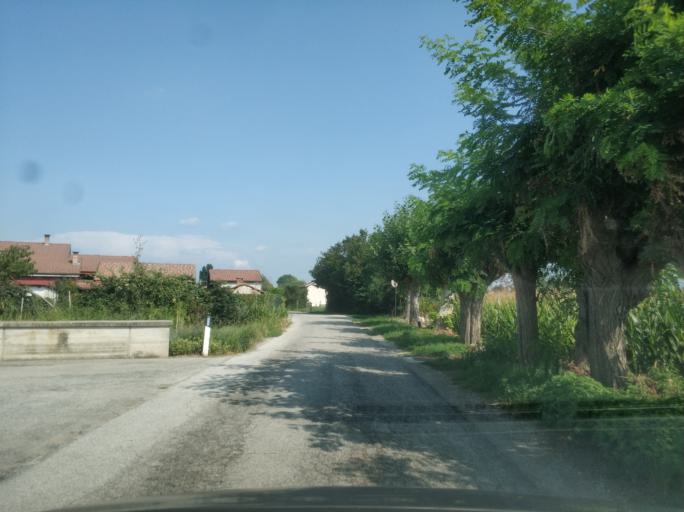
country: IT
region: Piedmont
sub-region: Provincia di Cuneo
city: Roata Rossi
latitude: 44.4539
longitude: 7.4762
